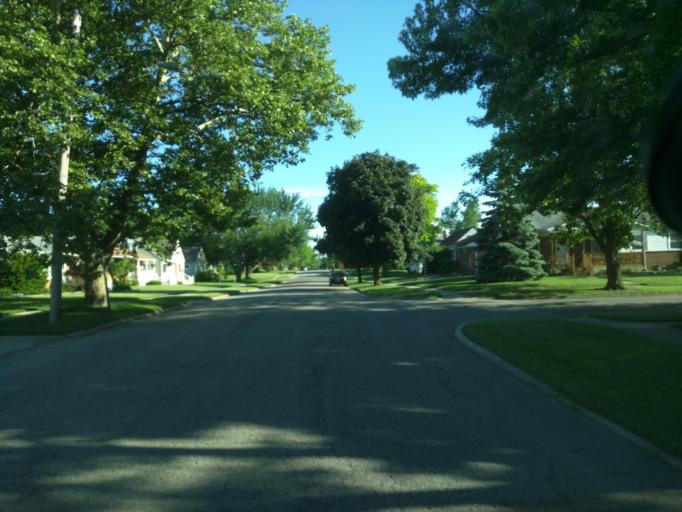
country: US
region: Michigan
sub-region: Ingham County
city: Edgemont Park
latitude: 42.7458
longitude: -84.5963
